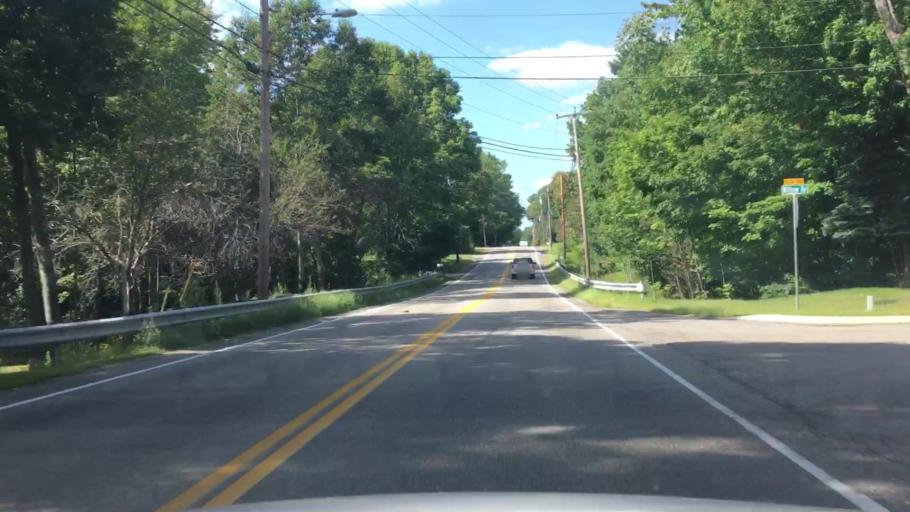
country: US
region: Maine
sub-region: Cumberland County
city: Westbrook
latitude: 43.7328
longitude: -70.3456
